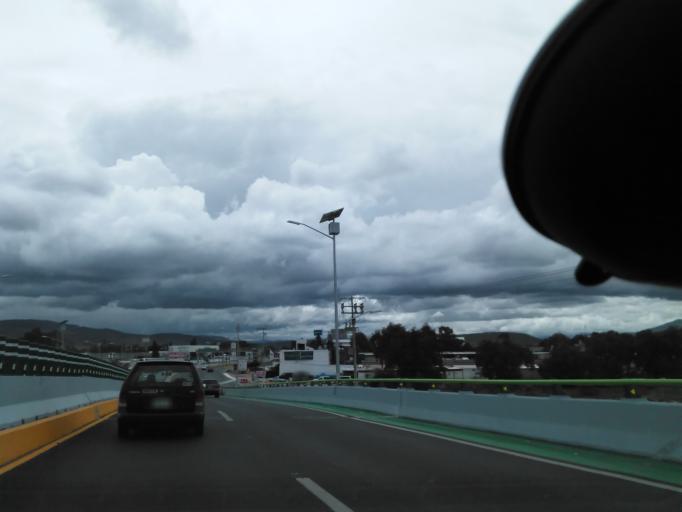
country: MX
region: Hidalgo
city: El Llano
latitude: 20.0538
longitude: -99.3115
